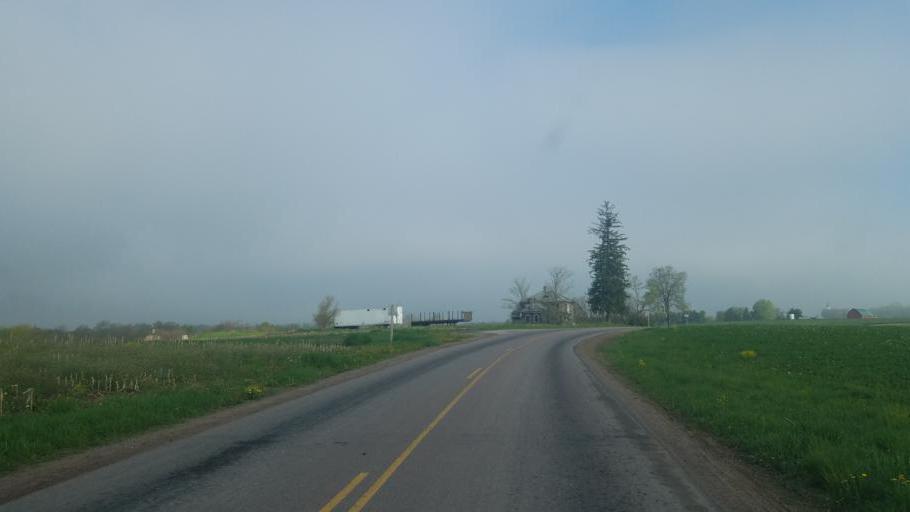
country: US
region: Wisconsin
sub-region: Vernon County
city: Hillsboro
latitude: 43.6154
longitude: -90.4468
